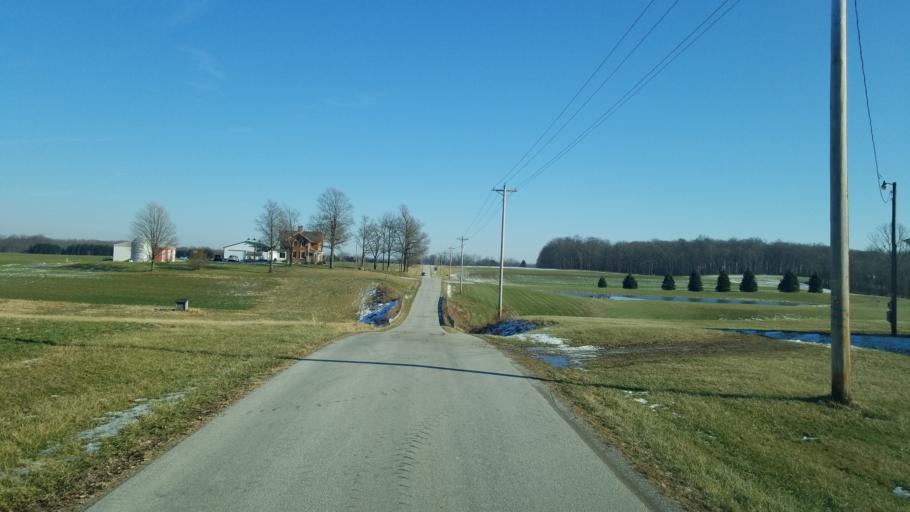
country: US
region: Ohio
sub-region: Huron County
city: Willard
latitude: 41.0902
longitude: -82.6750
